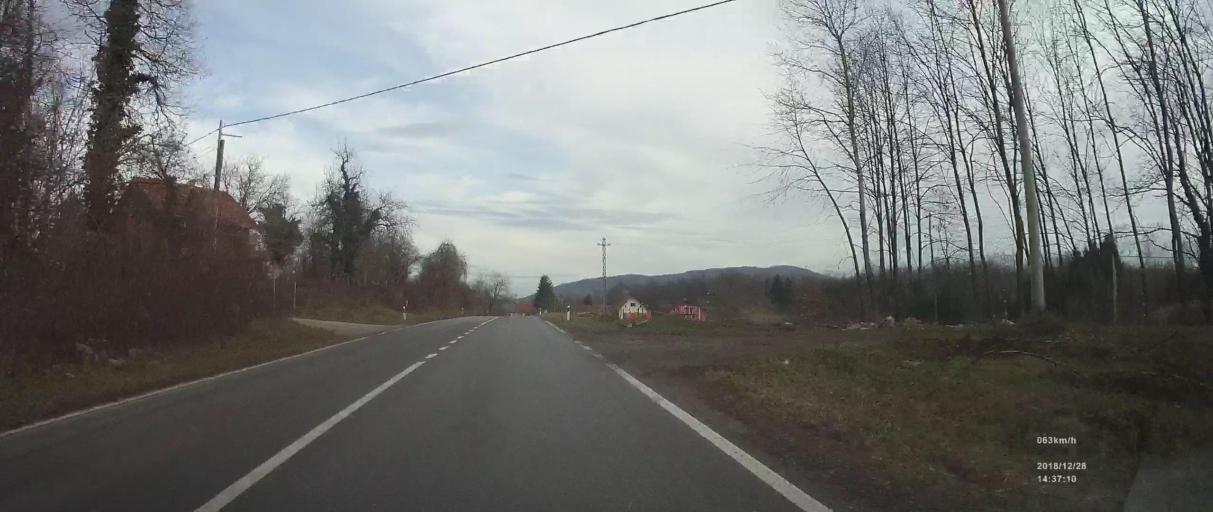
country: HR
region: Primorsko-Goranska
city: Vrbovsko
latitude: 45.4207
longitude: 15.2062
